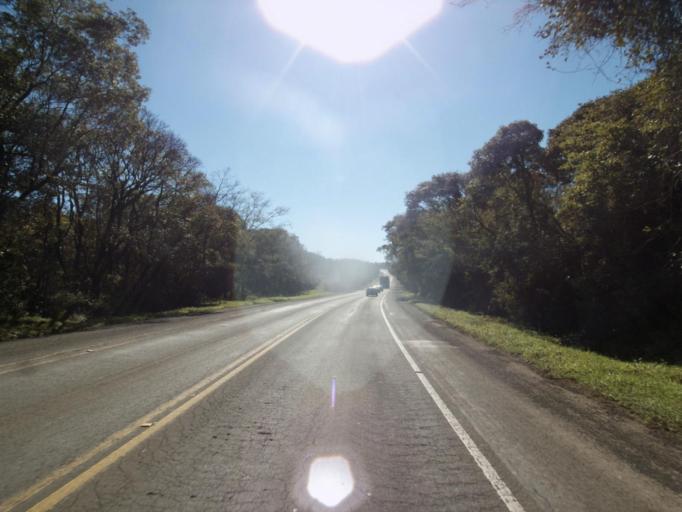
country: AR
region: Misiones
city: Bernardo de Irigoyen
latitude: -26.7907
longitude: -53.4575
